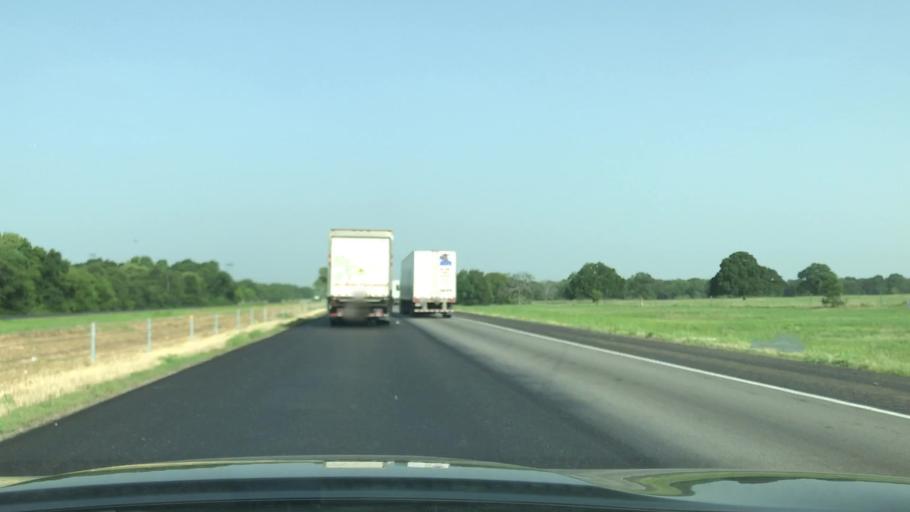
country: US
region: Texas
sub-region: Kaufman County
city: Terrell
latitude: 32.6718
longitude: -96.1581
